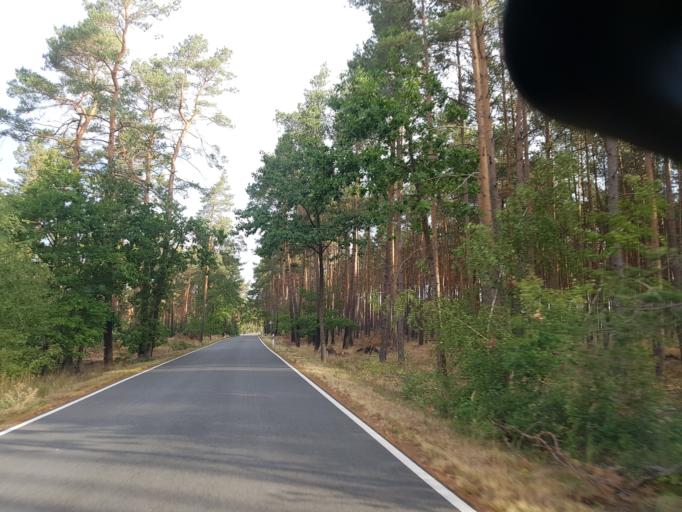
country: DE
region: Saxony-Anhalt
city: Holzdorf
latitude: 51.7934
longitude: 13.1028
